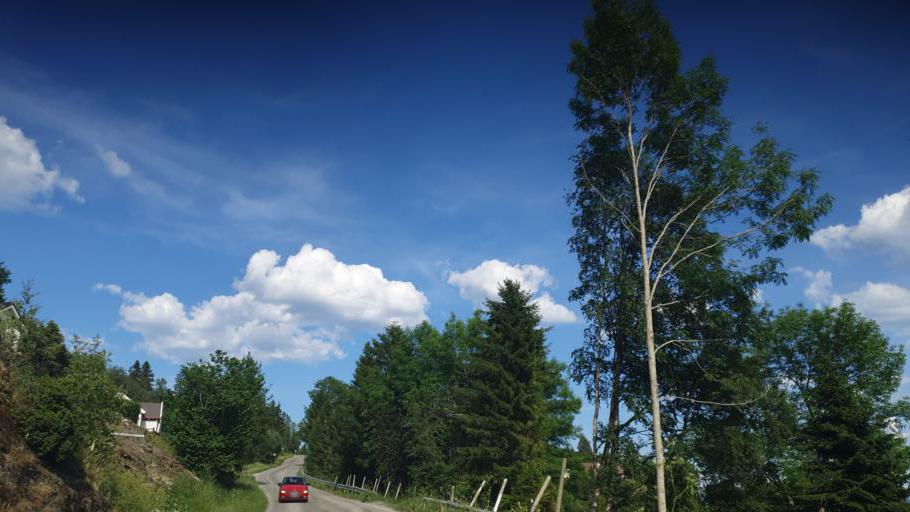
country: NO
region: Nord-Trondelag
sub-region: Leksvik
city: Leksvik
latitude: 63.6782
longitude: 10.6520
